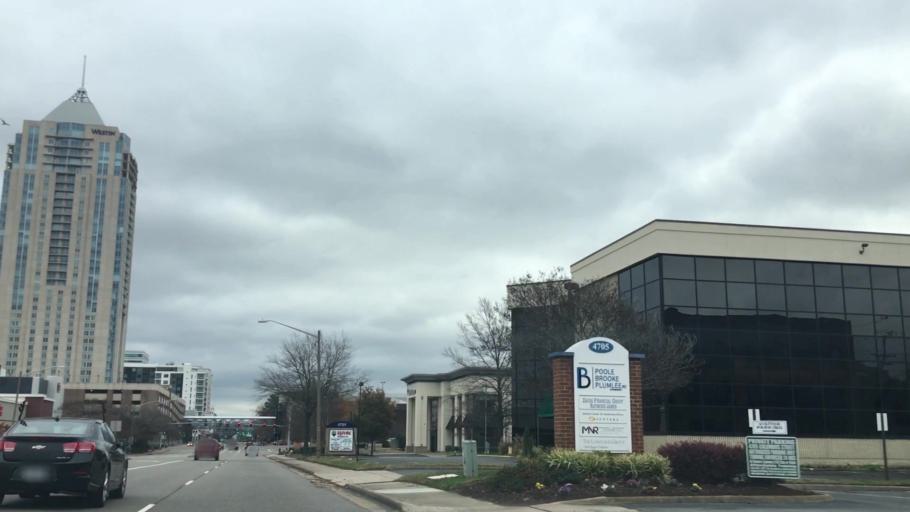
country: US
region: Virginia
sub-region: City of Chesapeake
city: Chesapeake
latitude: 36.8410
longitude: -76.1399
